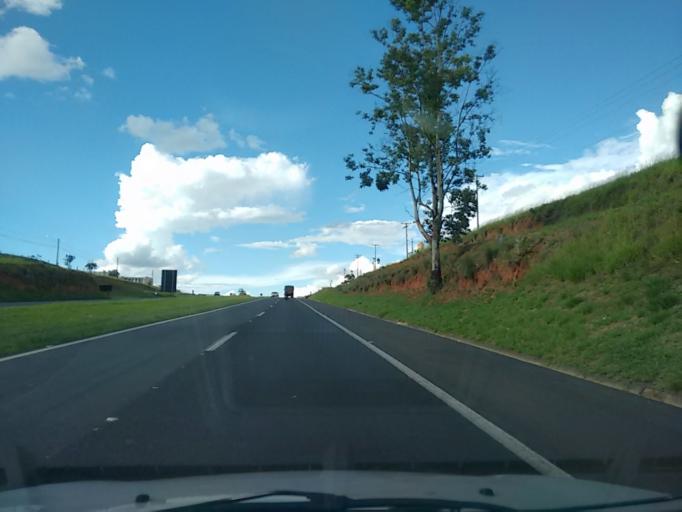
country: BR
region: Sao Paulo
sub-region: Sao Carlos
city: Sao Carlos
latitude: -22.0299
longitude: -47.8596
